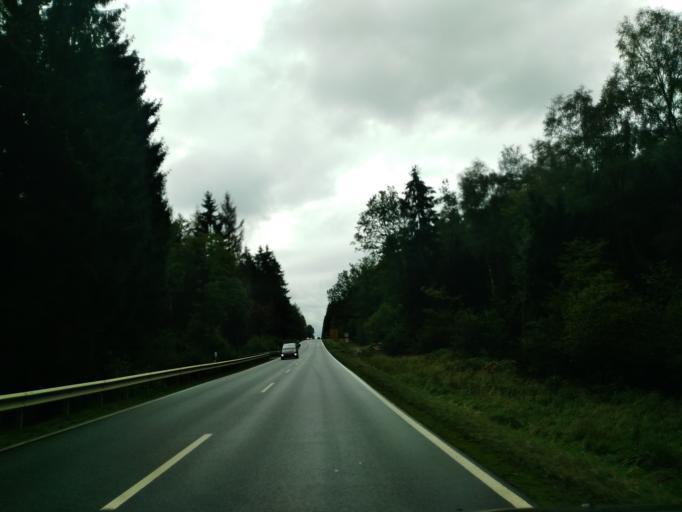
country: DE
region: Rheinland-Pfalz
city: Windhagen
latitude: 50.6346
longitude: 7.3058
